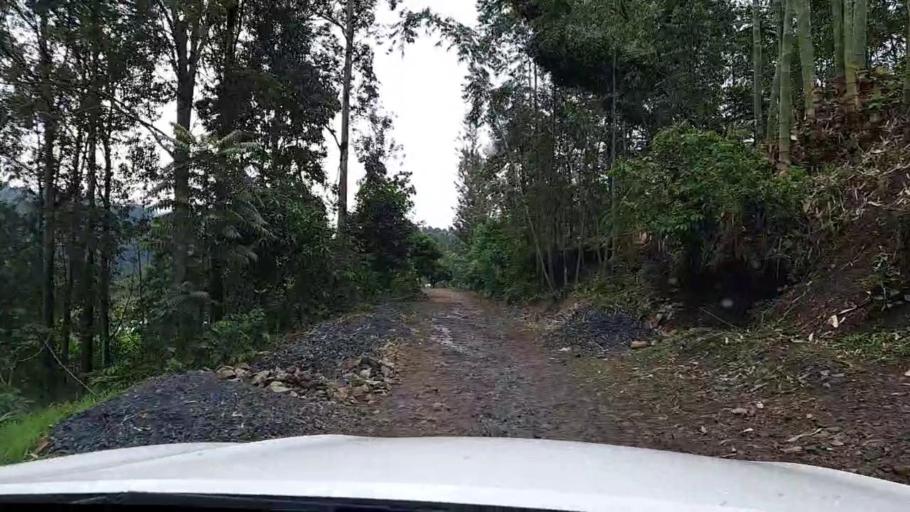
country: RW
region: Western Province
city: Cyangugu
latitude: -2.5434
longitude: 29.0384
